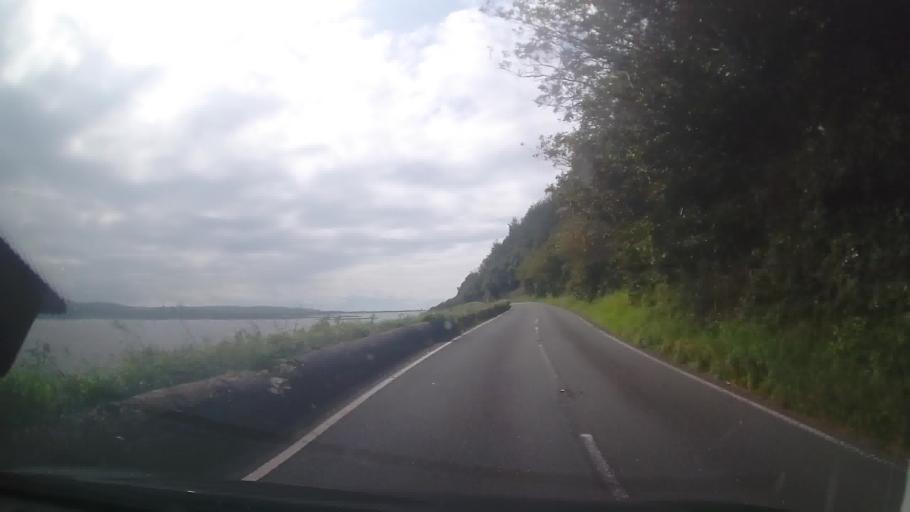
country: GB
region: Wales
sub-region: Sir Powys
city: Machynlleth
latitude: 52.5584
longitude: -3.9665
